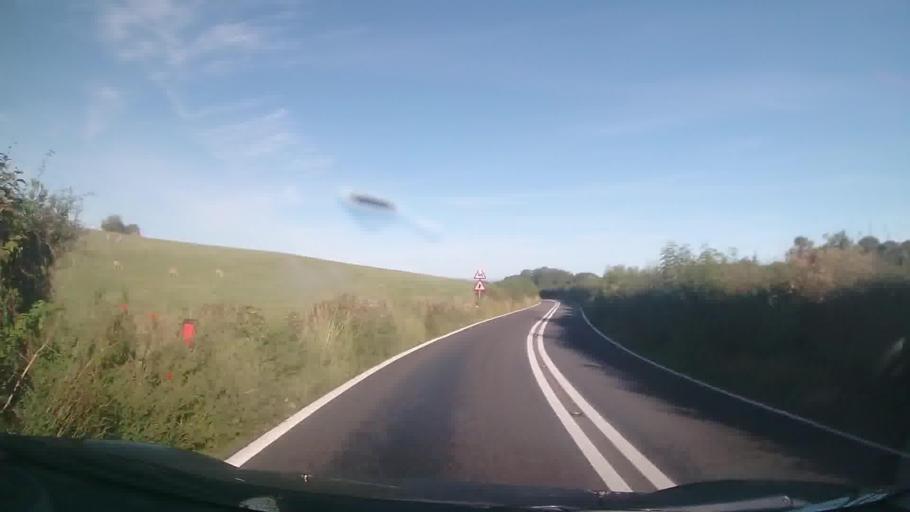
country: GB
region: Wales
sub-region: Sir Powys
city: Hay
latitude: 51.9679
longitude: -3.2142
